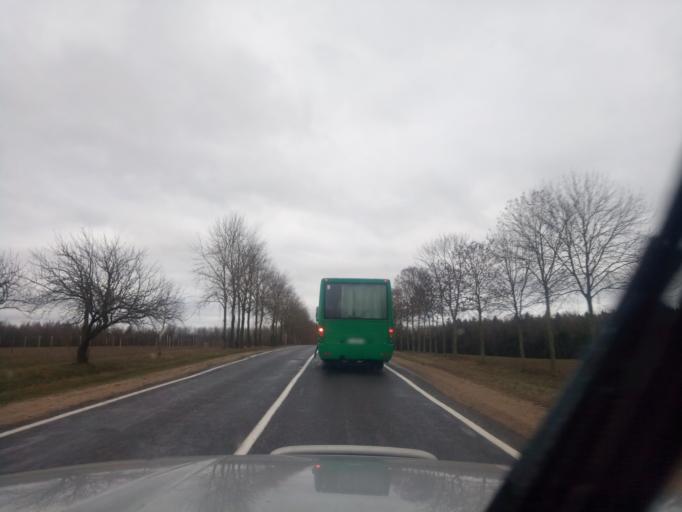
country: BY
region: Minsk
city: Kapyl'
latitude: 53.1713
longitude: 27.1486
